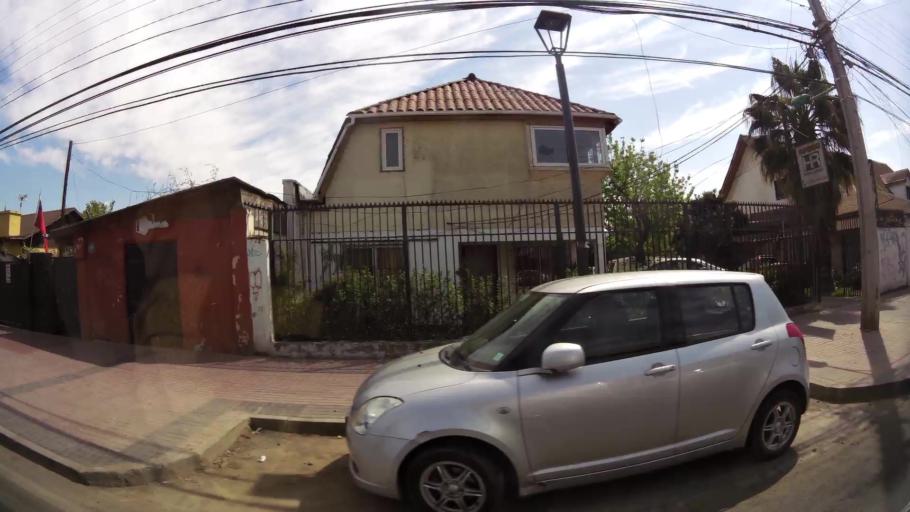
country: CL
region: Santiago Metropolitan
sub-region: Provincia de Talagante
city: Talagante
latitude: -33.6622
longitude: -70.9276
